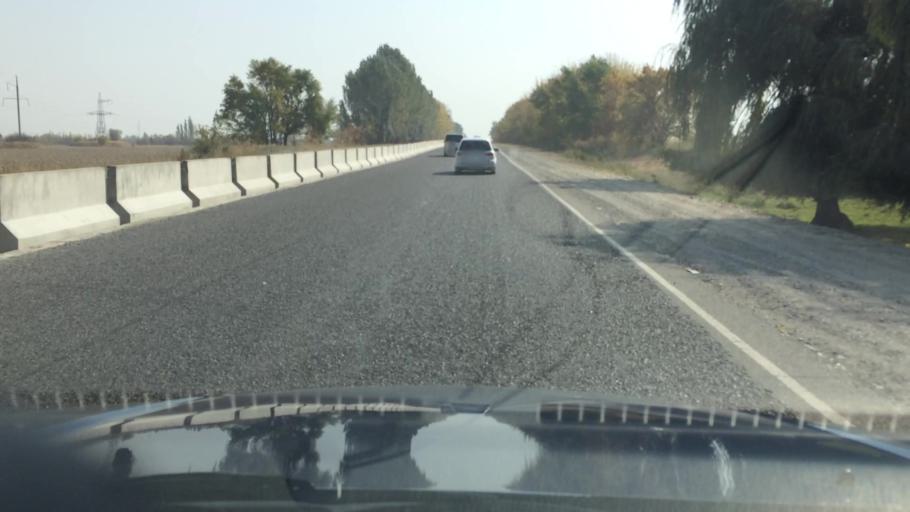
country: KG
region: Chuy
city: Kant
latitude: 42.9654
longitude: 74.9125
